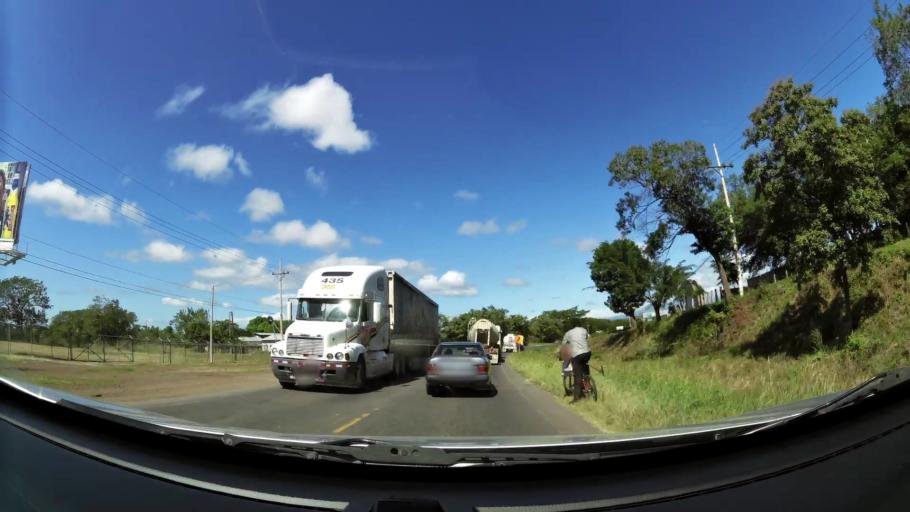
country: CR
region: Guanacaste
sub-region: Canton de Canas
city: Canas
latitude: 10.4139
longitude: -85.0865
